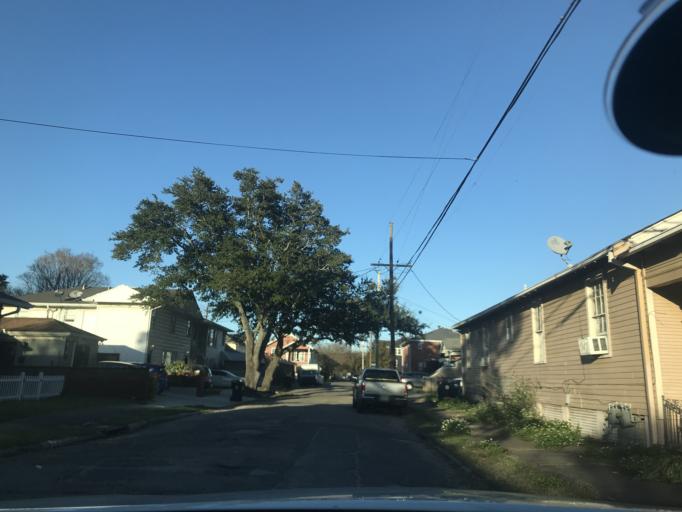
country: US
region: Louisiana
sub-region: Orleans Parish
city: New Orleans
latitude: 29.9515
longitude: -90.1072
